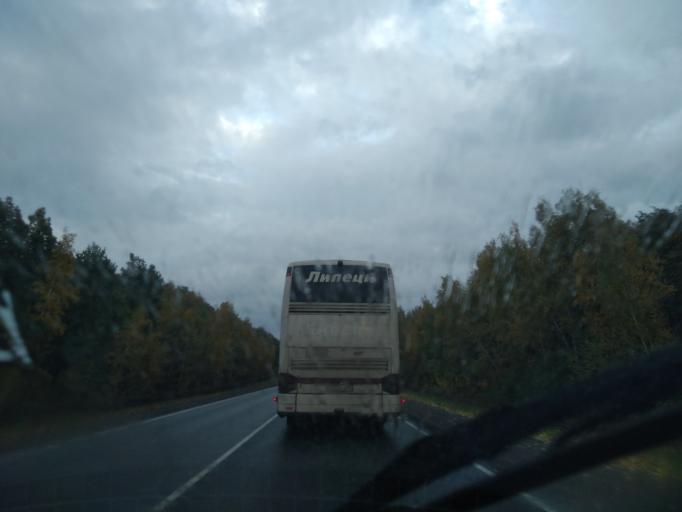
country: RU
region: Lipetsk
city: Borinskoye
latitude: 52.5985
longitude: 39.3097
